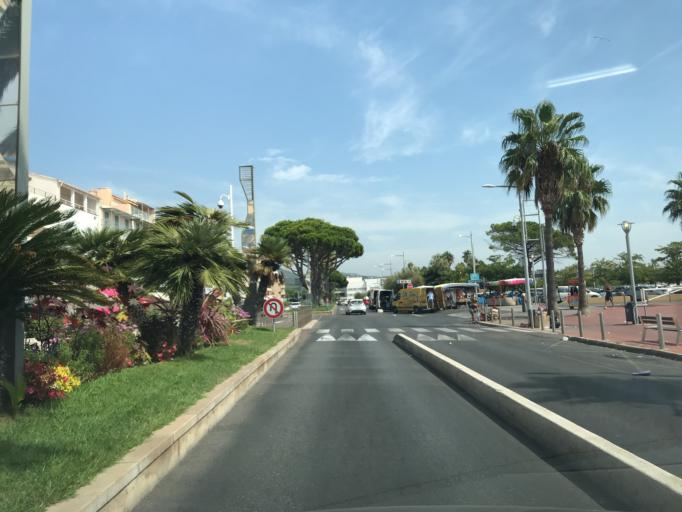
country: FR
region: Provence-Alpes-Cote d'Azur
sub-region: Departement du Var
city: Bandol
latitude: 43.1362
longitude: 5.7568
